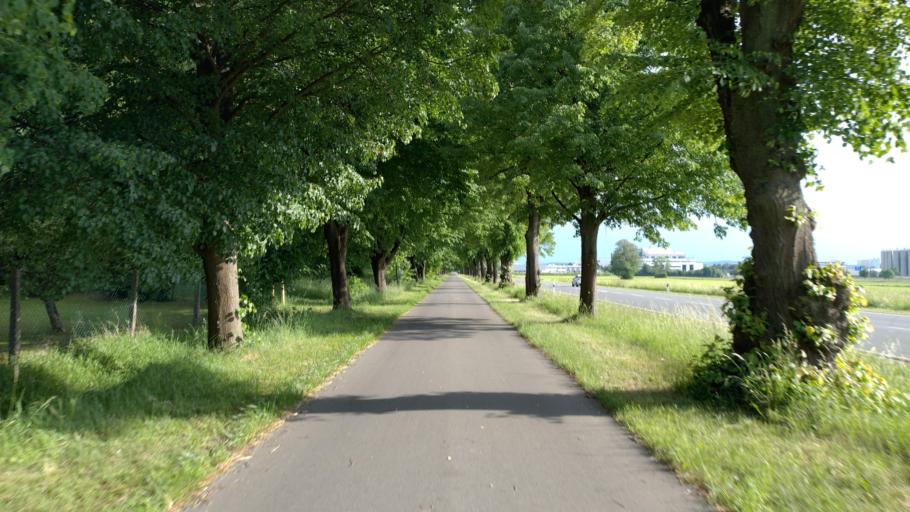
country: DE
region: Bavaria
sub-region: Upper Franconia
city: Bindlach
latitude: 49.9755
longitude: 11.6112
